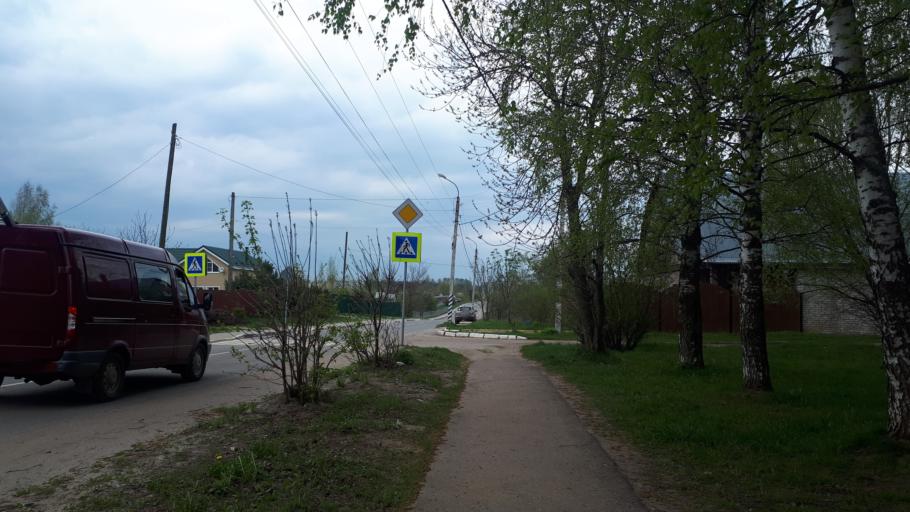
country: RU
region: Jaroslavl
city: Konstantinovskiy
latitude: 57.8318
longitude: 39.5909
